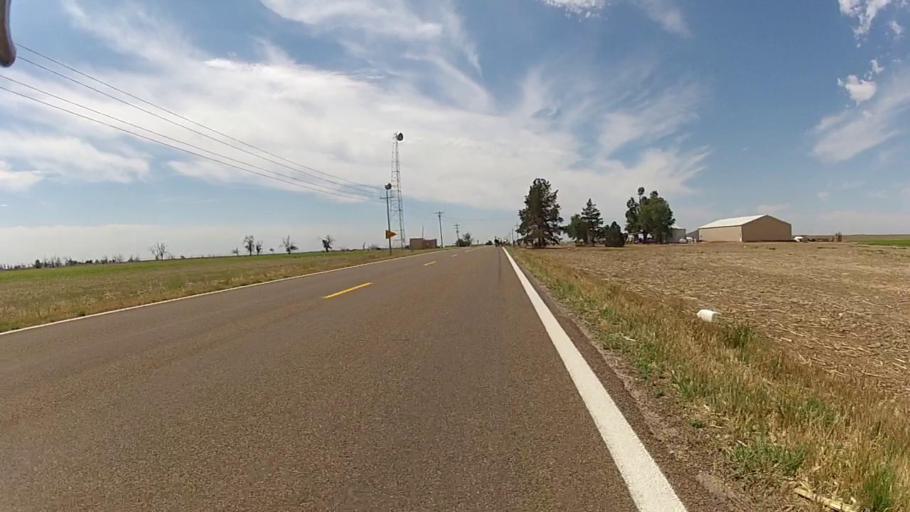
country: US
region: Kansas
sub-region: Haskell County
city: Satanta
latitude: 37.4943
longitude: -101.1078
